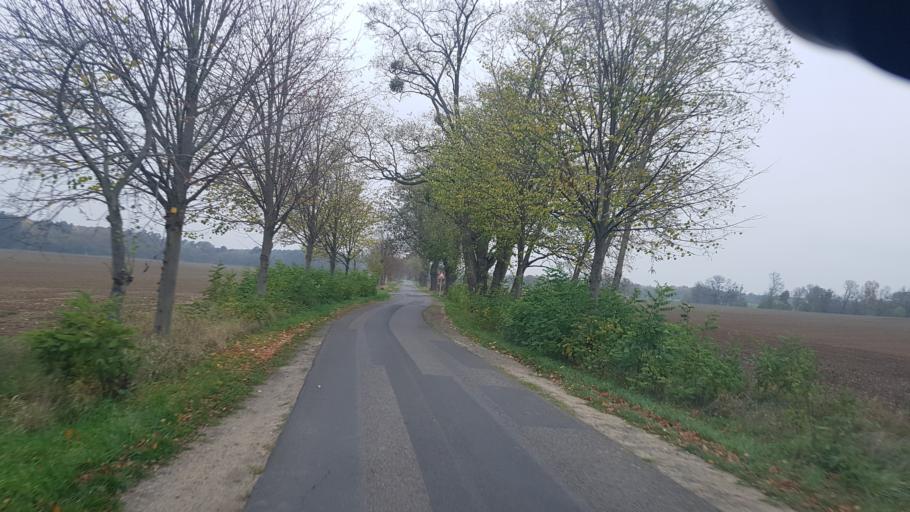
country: DE
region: Brandenburg
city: Lindow
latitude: 52.9404
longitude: 13.0608
